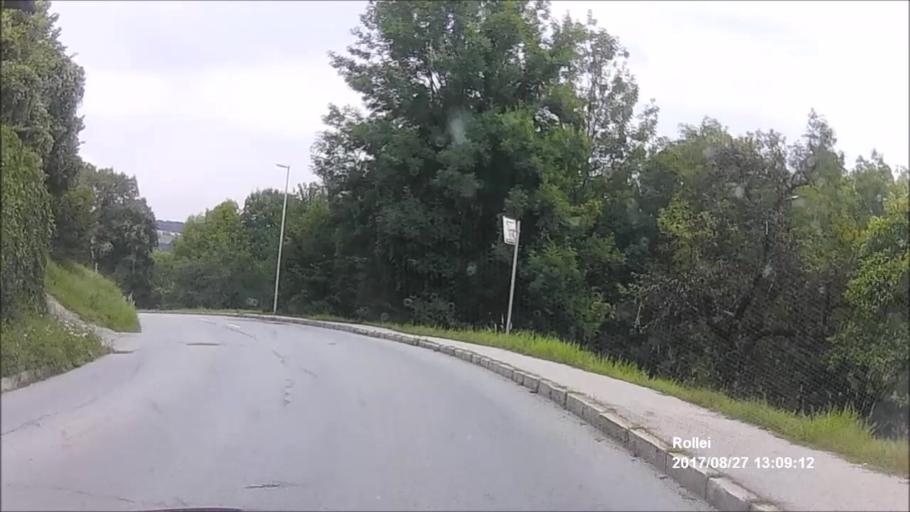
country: AT
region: Upper Austria
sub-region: Politischer Bezirk Scharding
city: Scharding
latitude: 48.5047
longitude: 13.4478
